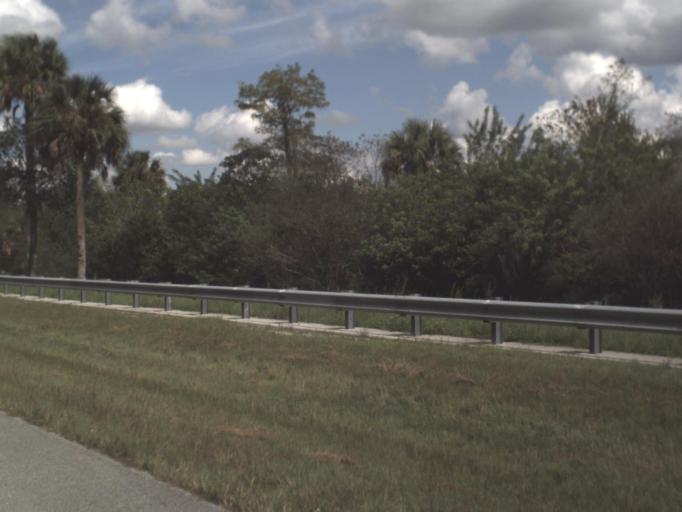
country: US
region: Florida
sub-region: Collier County
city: Lely Resort
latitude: 26.0030
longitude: -81.3467
